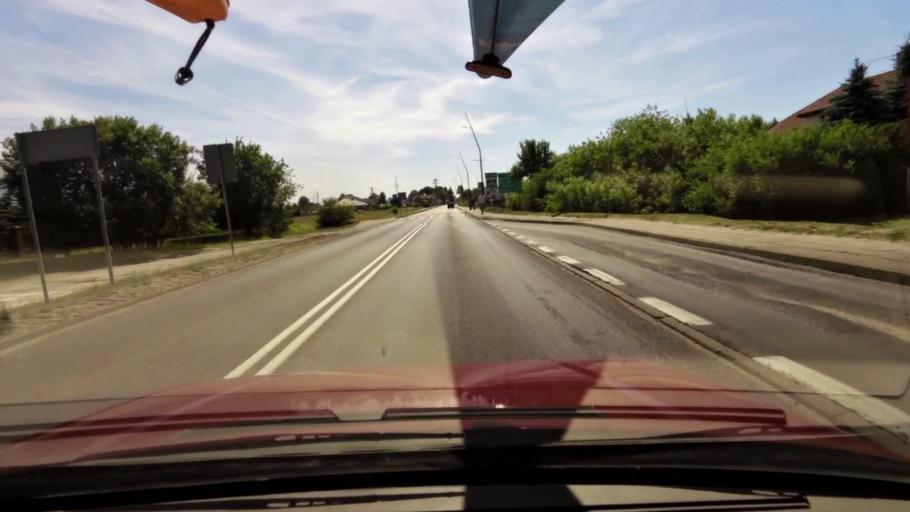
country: PL
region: Pomeranian Voivodeship
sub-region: Powiat slupski
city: Kobylnica
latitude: 54.4482
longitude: 17.0103
